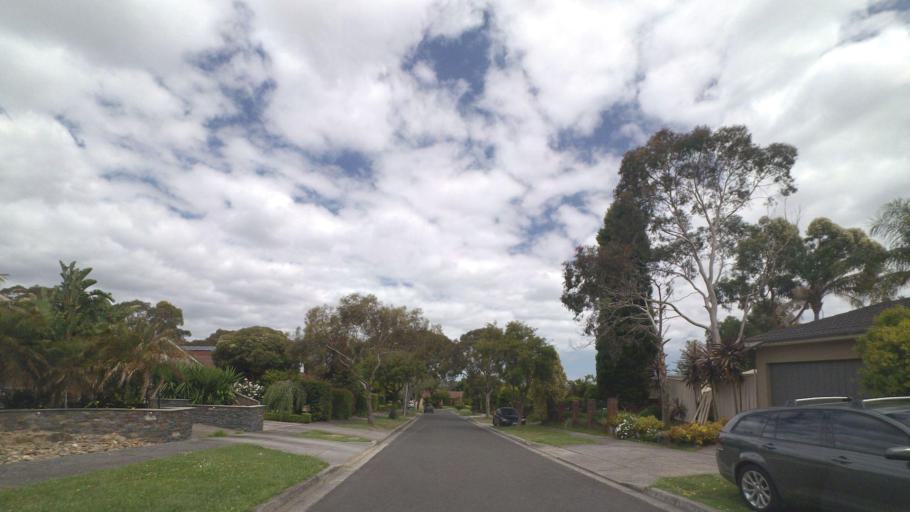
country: AU
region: Victoria
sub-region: Knox
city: Wantirna South
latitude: -37.8680
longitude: 145.2210
